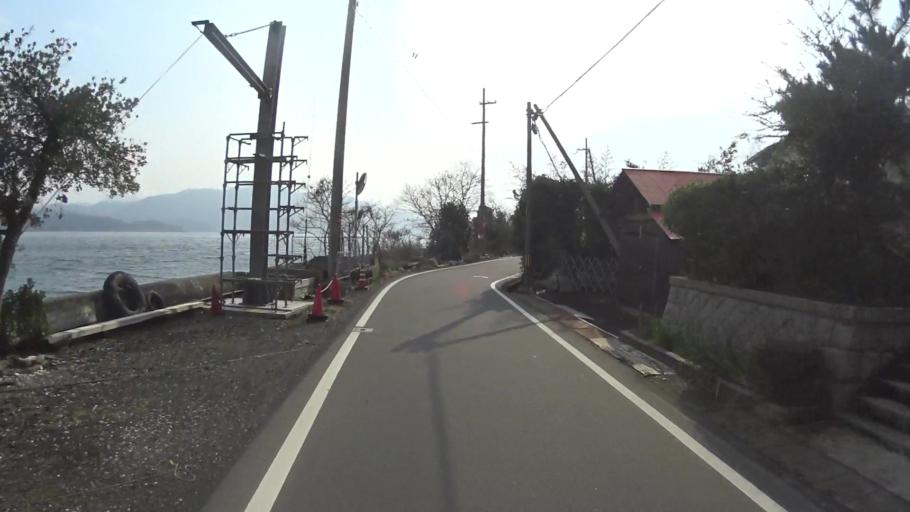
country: JP
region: Kyoto
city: Maizuru
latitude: 35.4959
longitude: 135.3321
